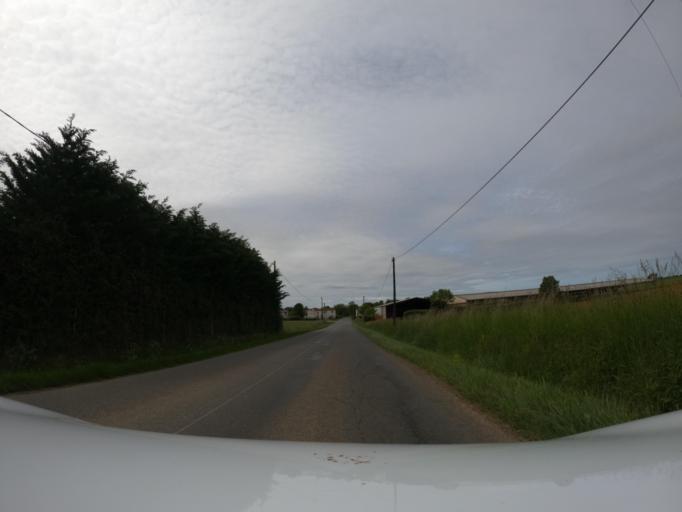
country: FR
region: Pays de la Loire
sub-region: Departement de la Vendee
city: Saint-Hilaire-des-Loges
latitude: 46.4943
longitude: -0.6658
